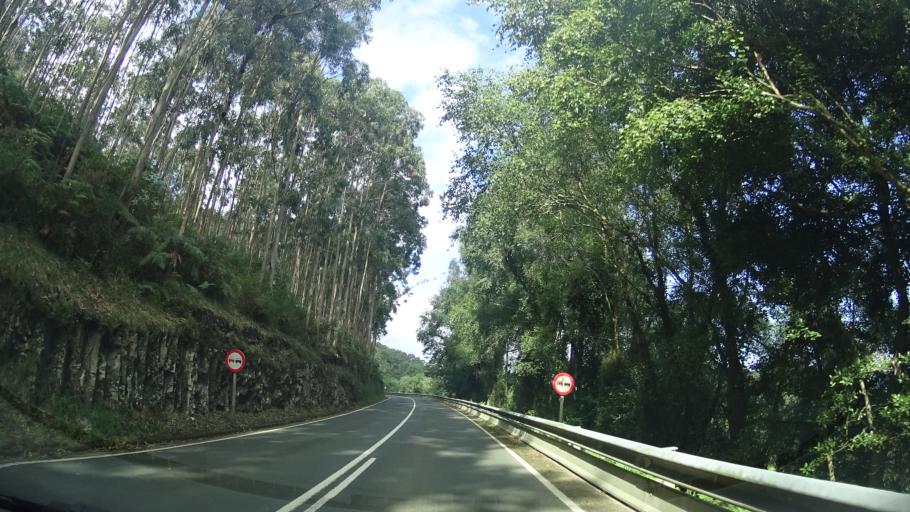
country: ES
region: Asturias
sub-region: Province of Asturias
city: Ribadesella
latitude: 43.4729
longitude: -5.1359
